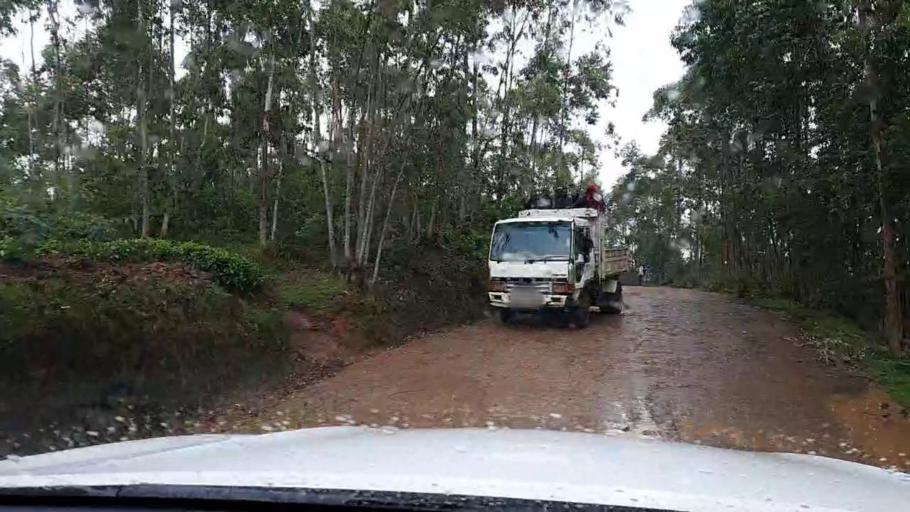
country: RW
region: Western Province
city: Cyangugu
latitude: -2.5482
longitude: 28.9790
